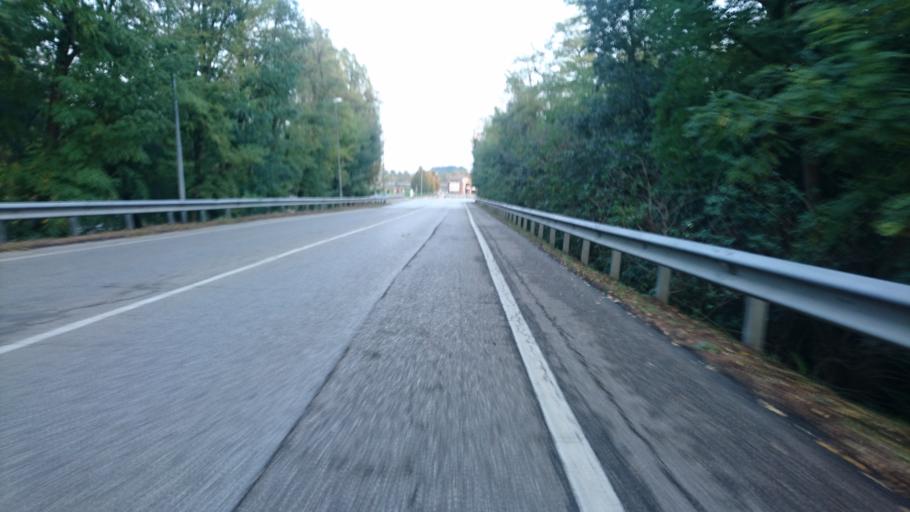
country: IT
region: Emilia-Romagna
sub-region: Provincia di Ferrara
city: Ferrara
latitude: 44.8596
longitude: 11.6113
